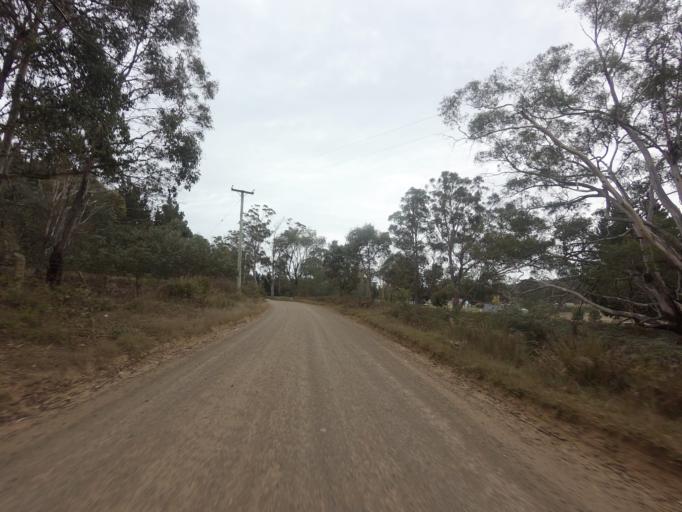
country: AU
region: Tasmania
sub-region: Derwent Valley
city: New Norfolk
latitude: -42.5780
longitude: 147.0025
